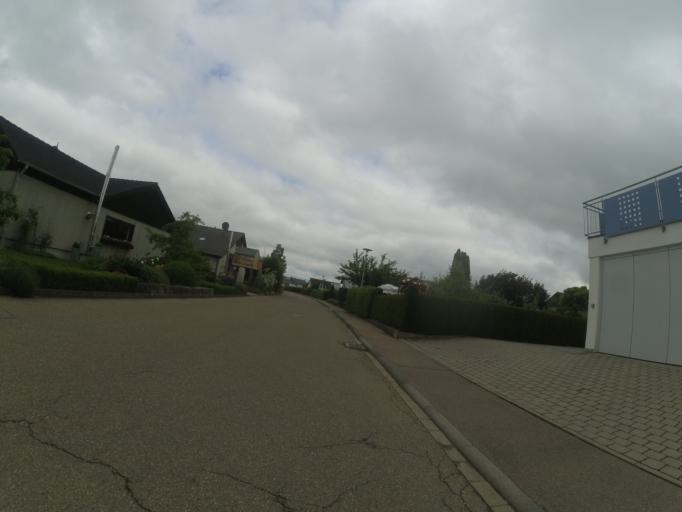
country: DE
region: Baden-Wuerttemberg
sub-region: Tuebingen Region
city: Bernstadt
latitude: 48.5015
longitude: 10.0271
